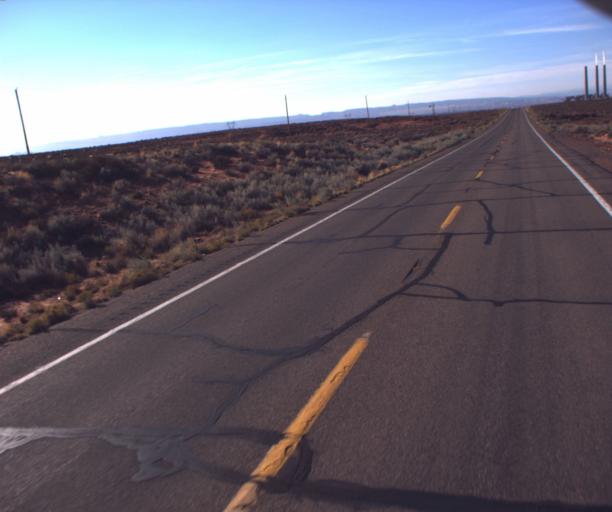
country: US
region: Arizona
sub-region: Coconino County
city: LeChee
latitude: 36.8826
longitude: -111.3528
